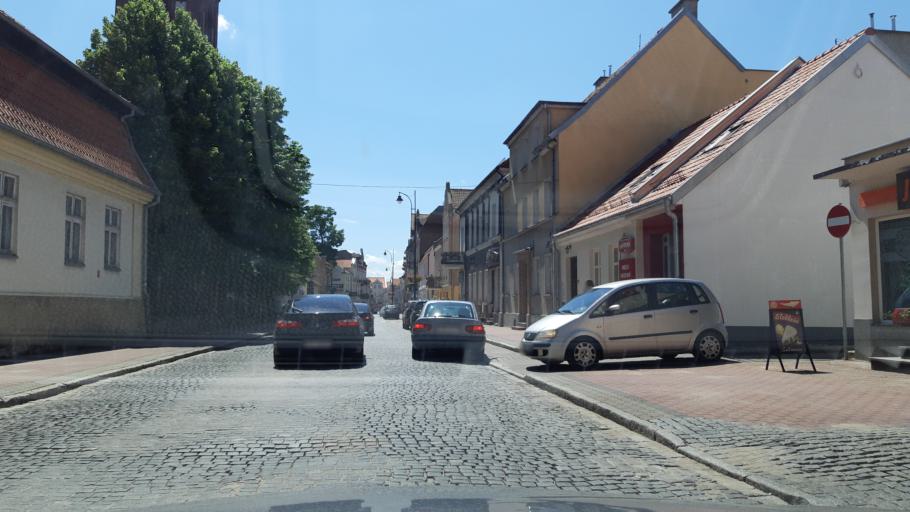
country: PL
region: Warmian-Masurian Voivodeship
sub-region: Powiat mragowski
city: Mragowo
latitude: 53.8740
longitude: 21.3041
